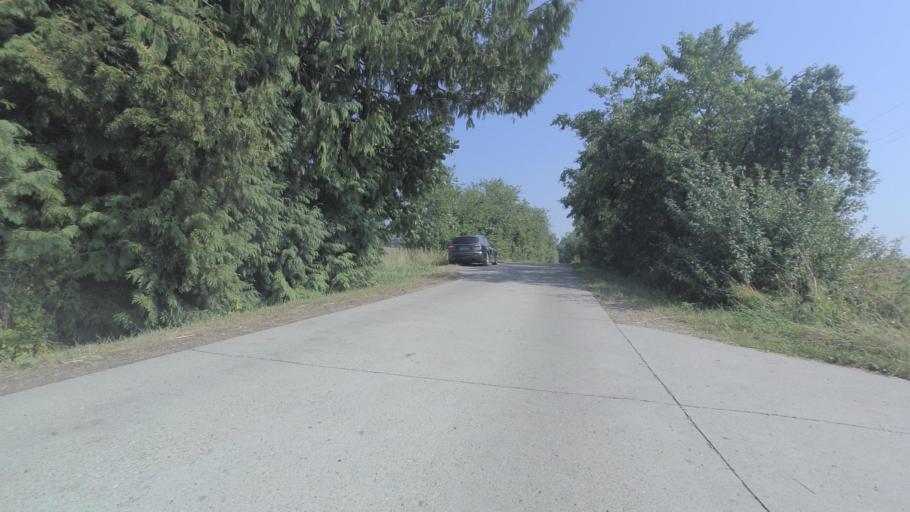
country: DE
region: Mecklenburg-Vorpommern
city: Pampow
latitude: 53.7209
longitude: 12.6410
